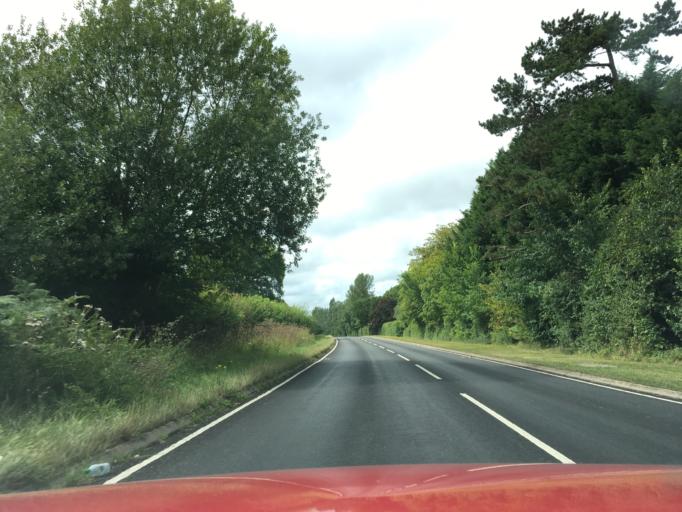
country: GB
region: England
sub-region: Kent
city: Cranbrook
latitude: 51.1098
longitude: 0.5428
